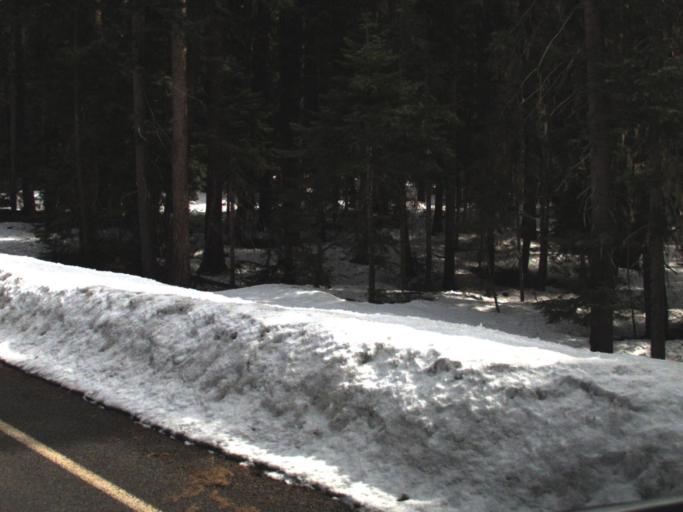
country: US
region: Washington
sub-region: Kittitas County
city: Cle Elum
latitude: 46.9422
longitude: -121.3350
